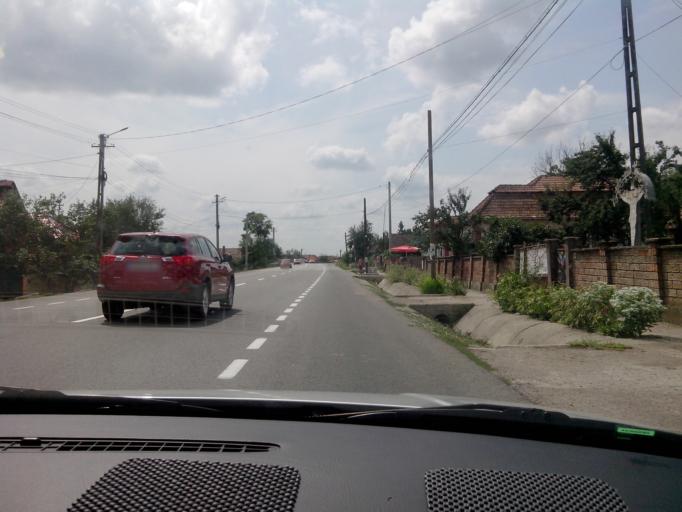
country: RO
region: Cluj
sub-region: Comuna Iclod
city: Iclod
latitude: 46.9523
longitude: 23.7956
